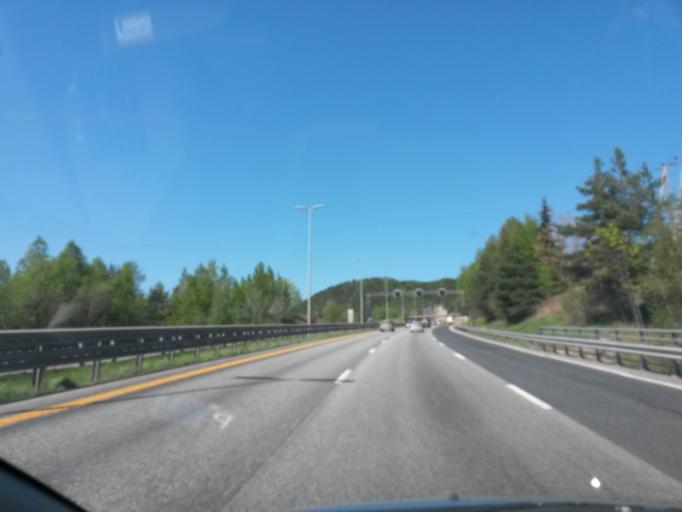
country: NO
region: Buskerud
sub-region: Lier
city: Tranby
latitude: 59.7843
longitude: 10.2733
